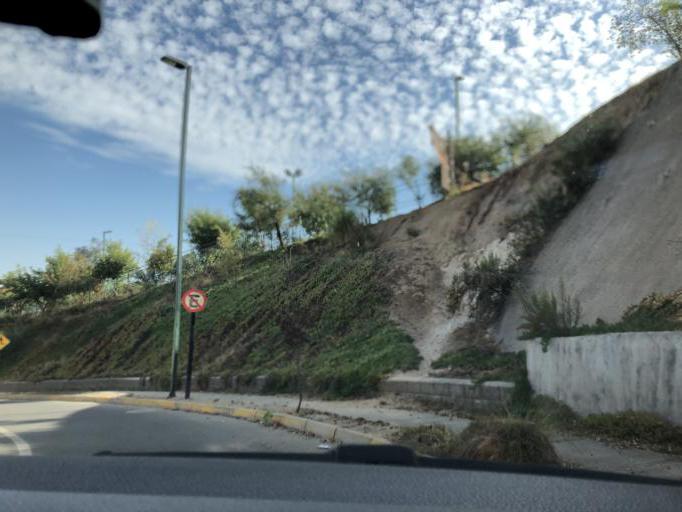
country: CL
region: Santiago Metropolitan
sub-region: Provincia de Cordillera
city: Puente Alto
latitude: -33.5929
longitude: -70.5337
